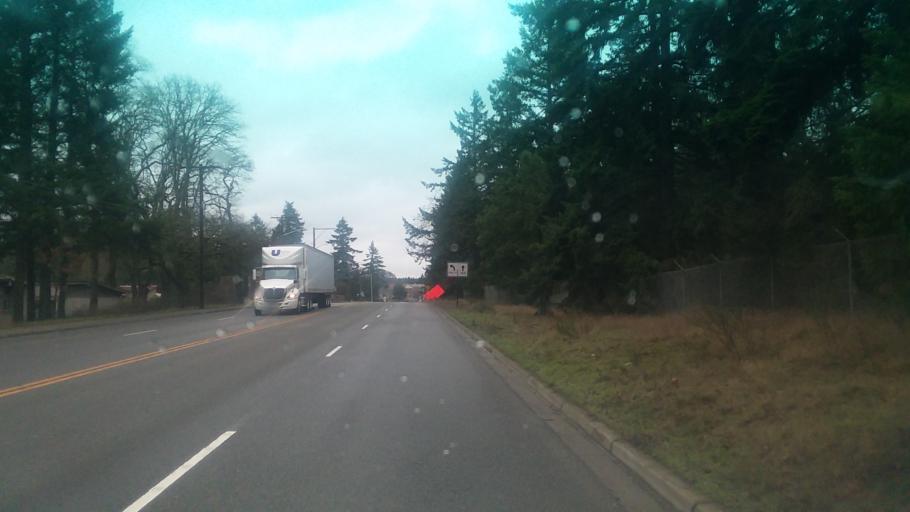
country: US
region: Washington
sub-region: Pierce County
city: Fort Lewis
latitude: 47.1230
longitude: -122.5429
